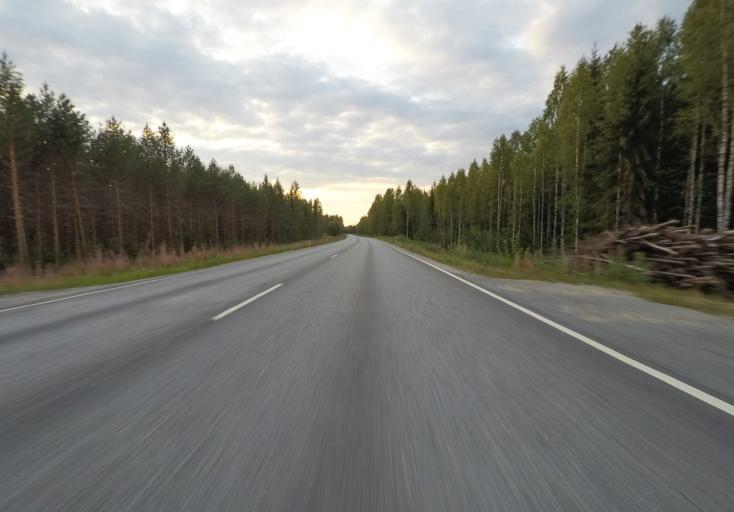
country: FI
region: Central Finland
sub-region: Jyvaeskylae
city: Toivakka
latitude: 62.2306
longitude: 26.1940
